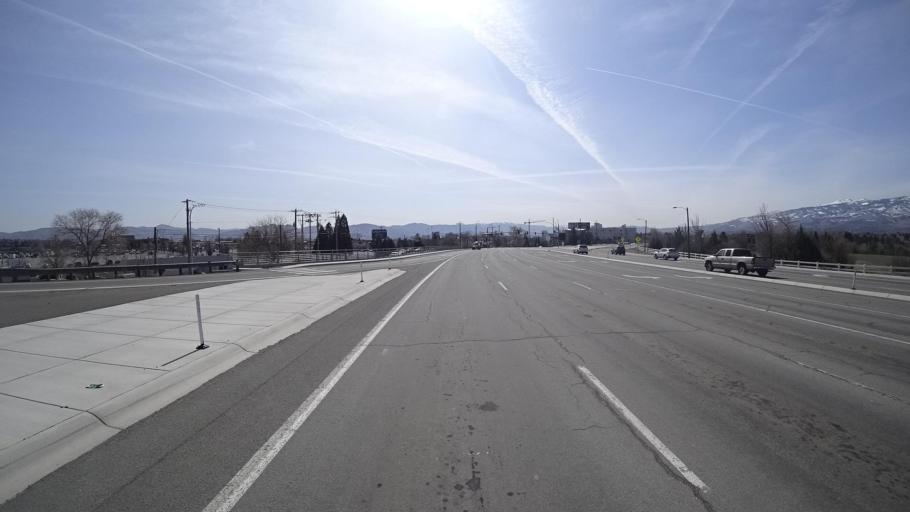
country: US
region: Nevada
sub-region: Washoe County
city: Reno
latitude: 39.5507
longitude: -119.8224
